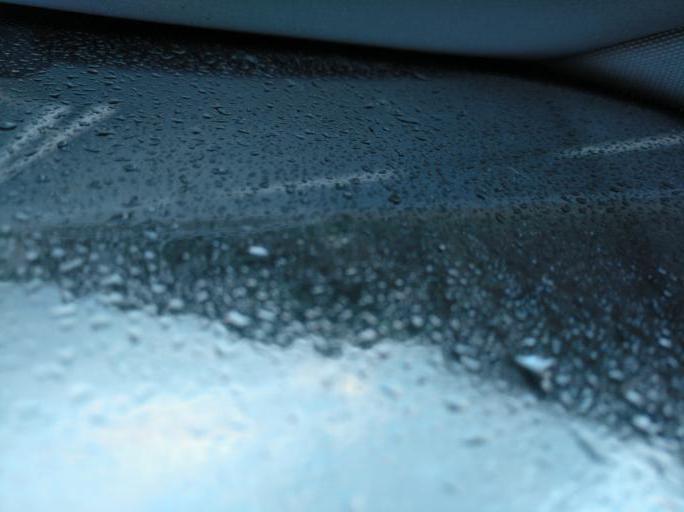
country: PT
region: Faro
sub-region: Castro Marim
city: Castro Marim
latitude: 37.2556
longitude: -7.4818
